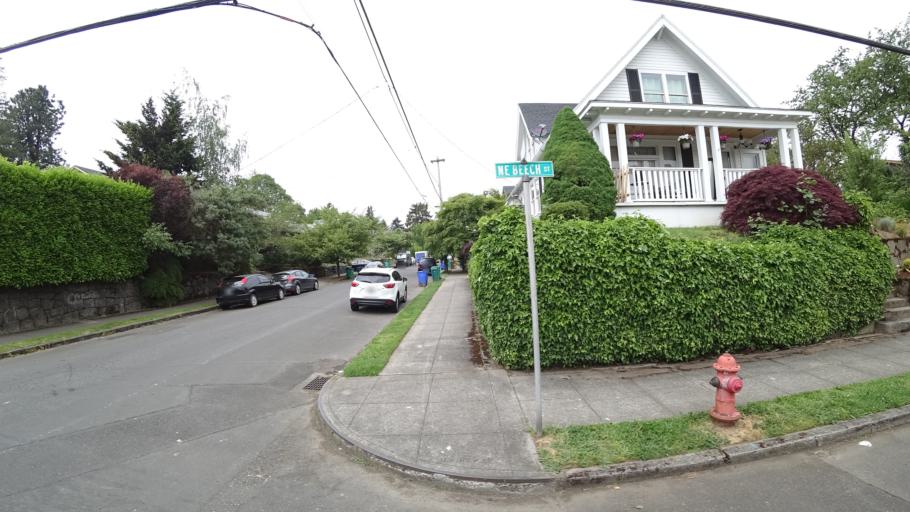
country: US
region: Oregon
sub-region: Multnomah County
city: Portland
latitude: 45.5495
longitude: -122.6576
